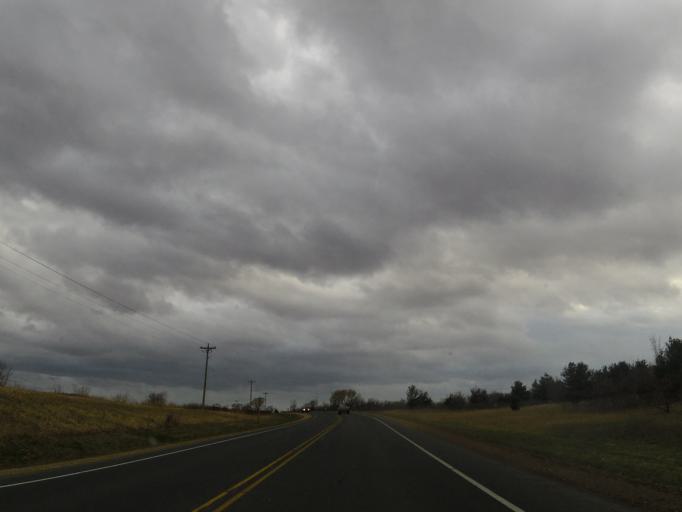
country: US
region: Wisconsin
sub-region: Saint Croix County
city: North Hudson
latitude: 45.0180
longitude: -92.6718
